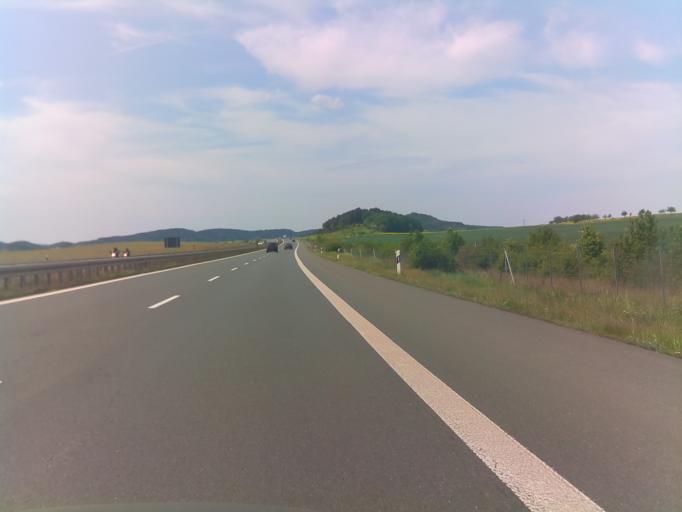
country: DE
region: Saxony-Anhalt
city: Westerhausen
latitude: 51.8133
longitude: 11.0976
